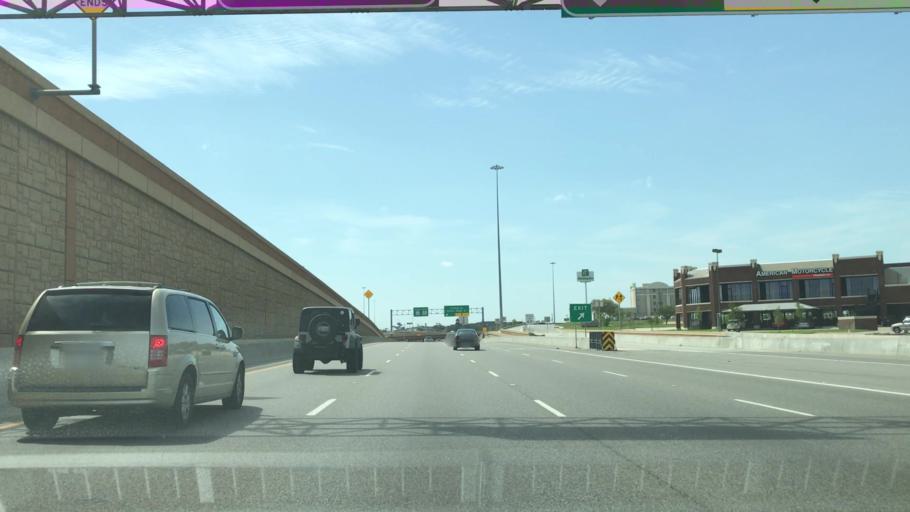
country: US
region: Texas
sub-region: Tarrant County
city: Bedford
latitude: 32.8380
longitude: -97.1144
